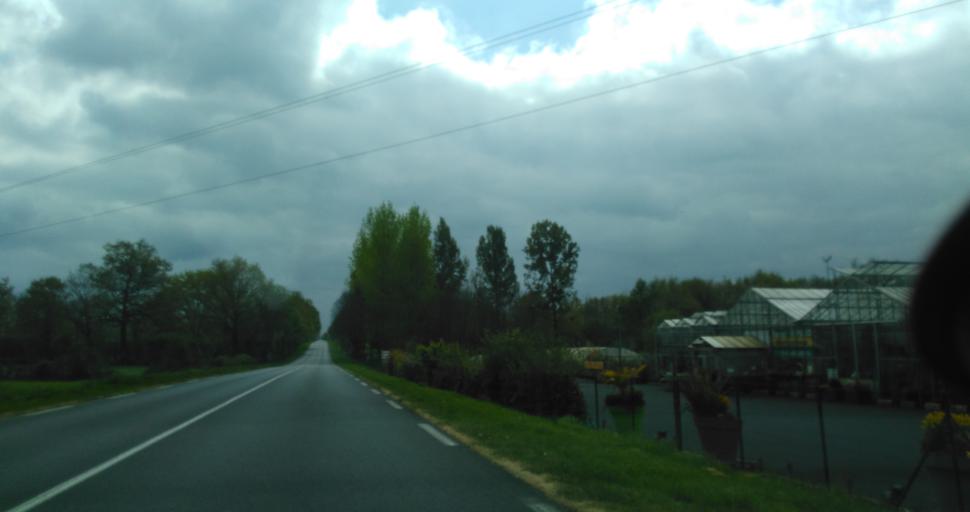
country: FR
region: Poitou-Charentes
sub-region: Departement des Deux-Sevres
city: Moncoutant
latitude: 46.7465
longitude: -0.6131
